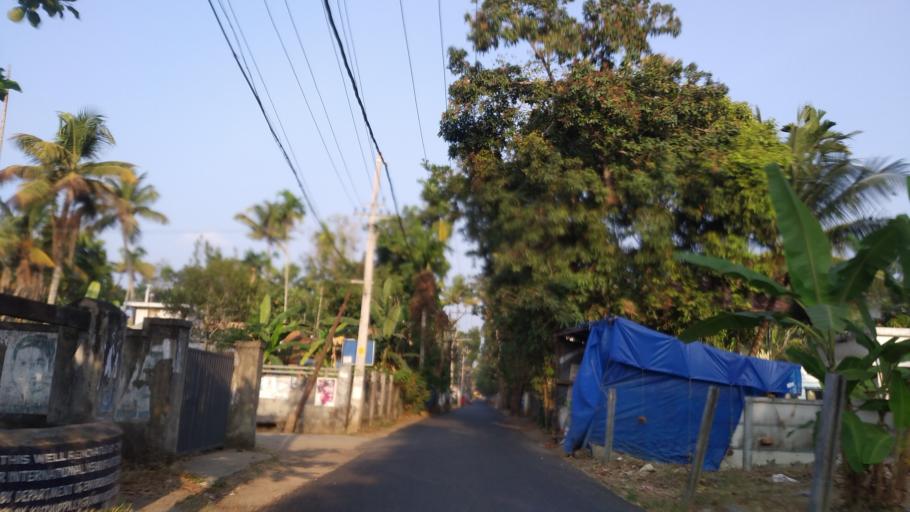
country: IN
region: Kerala
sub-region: Ernakulam
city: Elur
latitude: 10.1082
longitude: 76.1985
